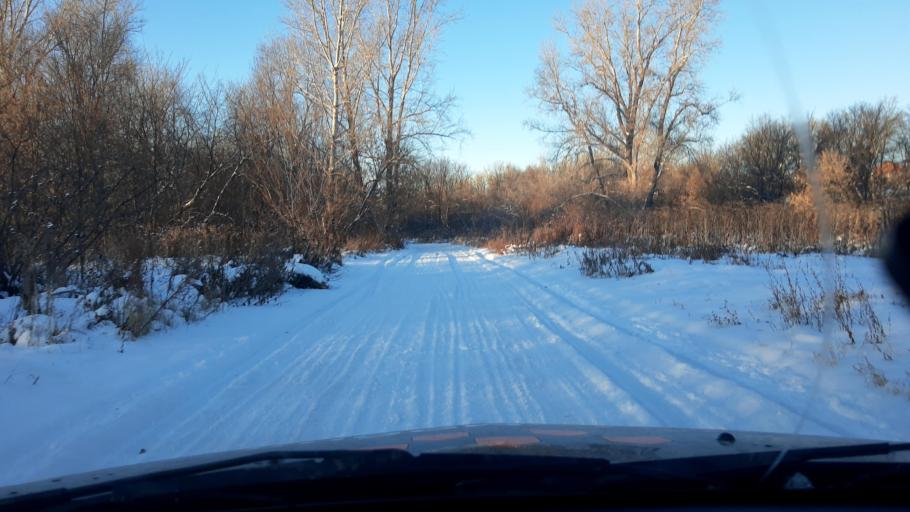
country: RU
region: Bashkortostan
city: Ufa
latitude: 54.6600
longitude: 55.9666
